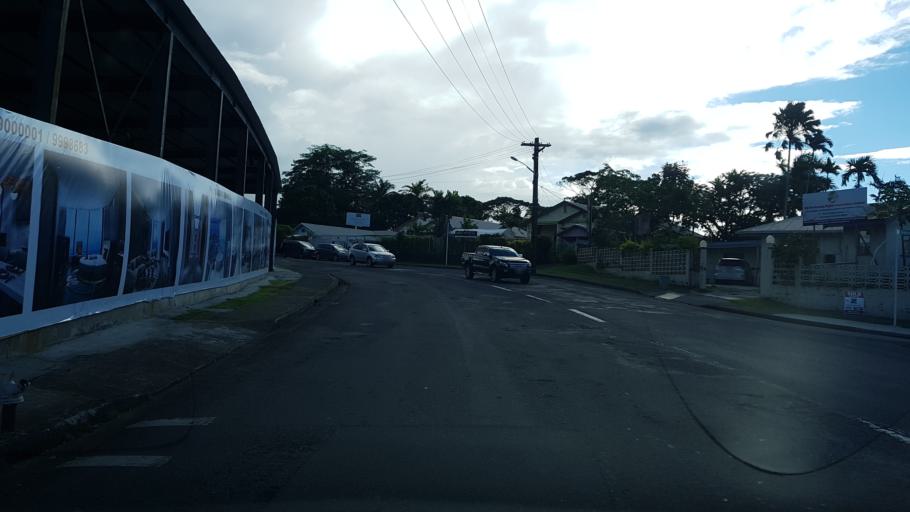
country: FJ
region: Central
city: Suva
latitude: -18.1468
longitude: 178.4308
